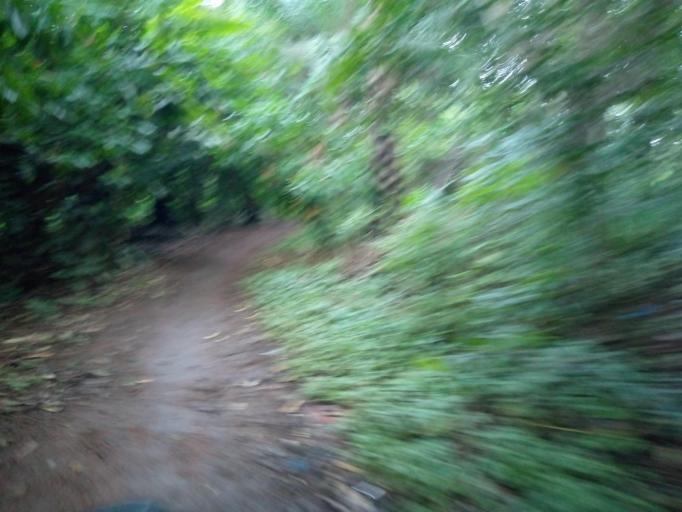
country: GN
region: Nzerekore
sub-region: Prefecture de Guekedou
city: Gueckedou
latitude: 8.4976
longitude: -10.3230
